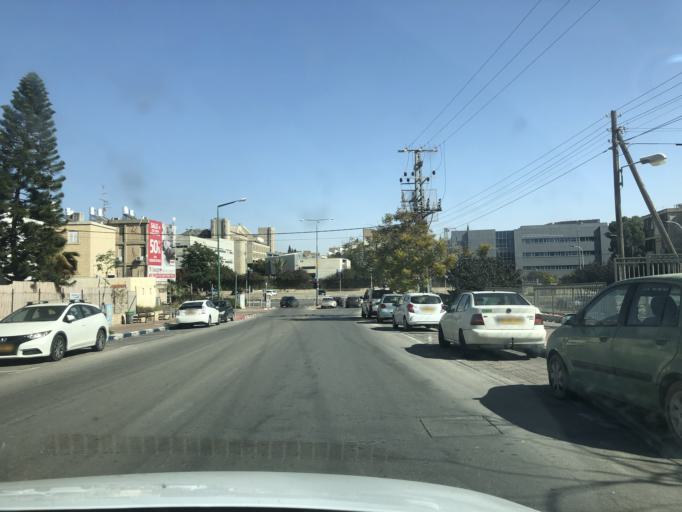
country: IL
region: Southern District
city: Beersheba
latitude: 31.2620
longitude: 34.7971
